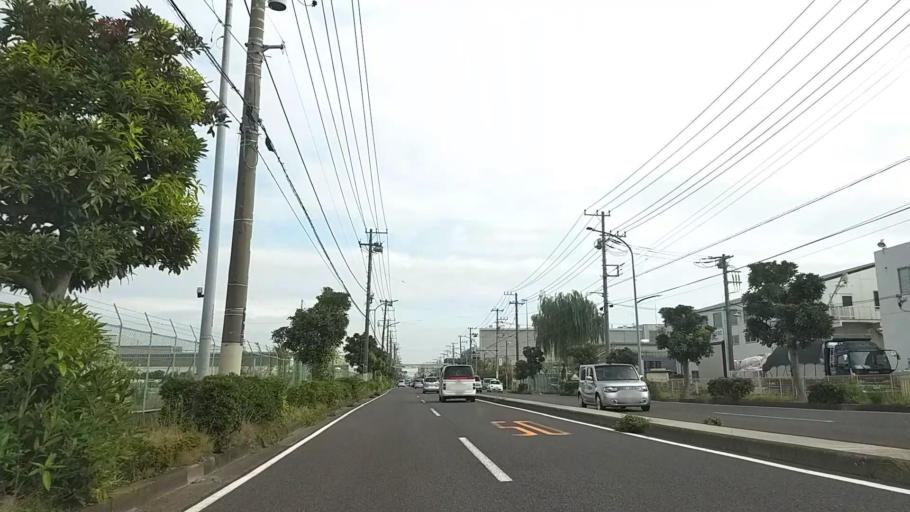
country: JP
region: Kanagawa
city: Hiratsuka
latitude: 35.3407
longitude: 139.3565
